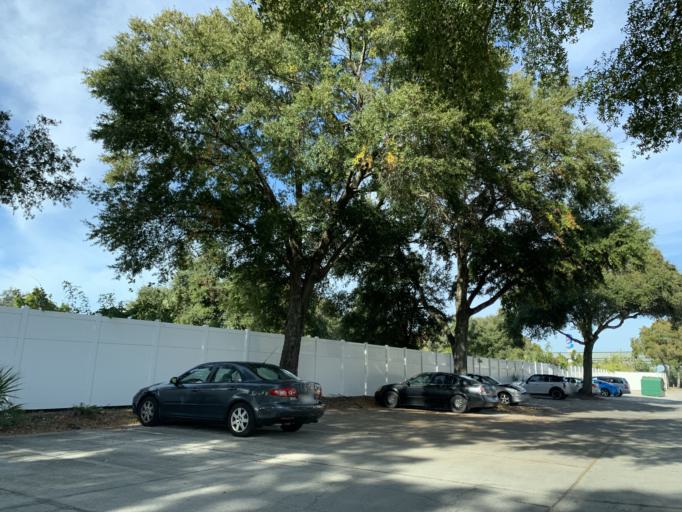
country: US
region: Florida
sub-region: Hillsborough County
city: Tampa
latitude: 27.8914
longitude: -82.5108
